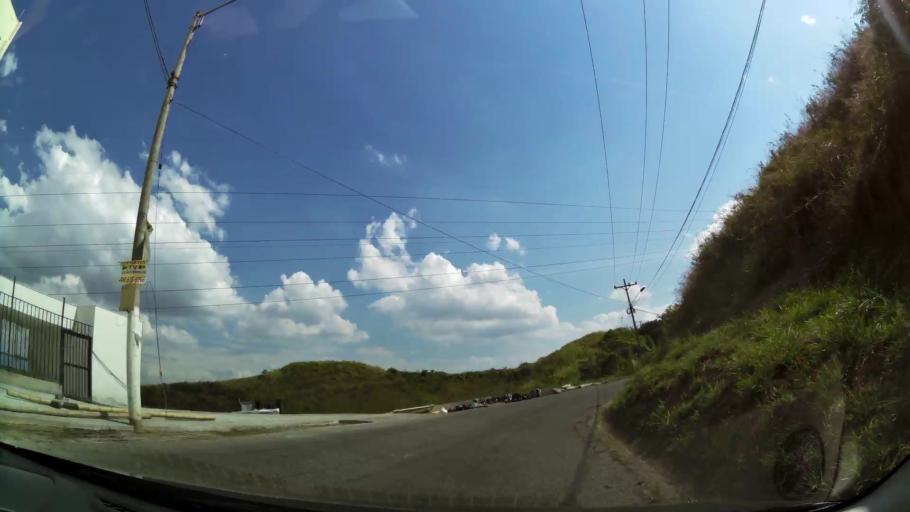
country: CO
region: Valle del Cauca
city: Cali
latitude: 3.4401
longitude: -76.5527
